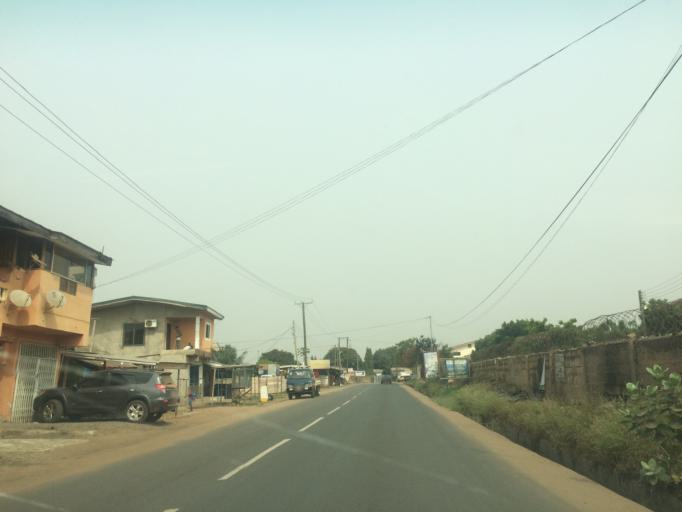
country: GH
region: Greater Accra
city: Nungua
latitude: 5.6067
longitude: -0.0861
